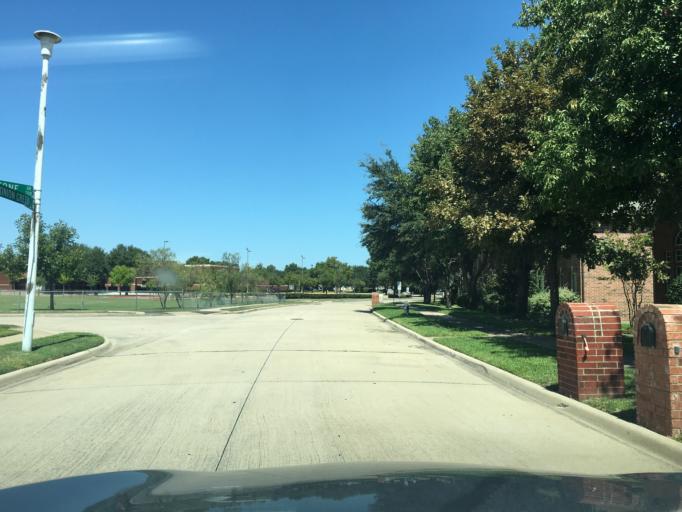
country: US
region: Texas
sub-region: Dallas County
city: Sachse
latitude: 32.9678
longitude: -96.6371
